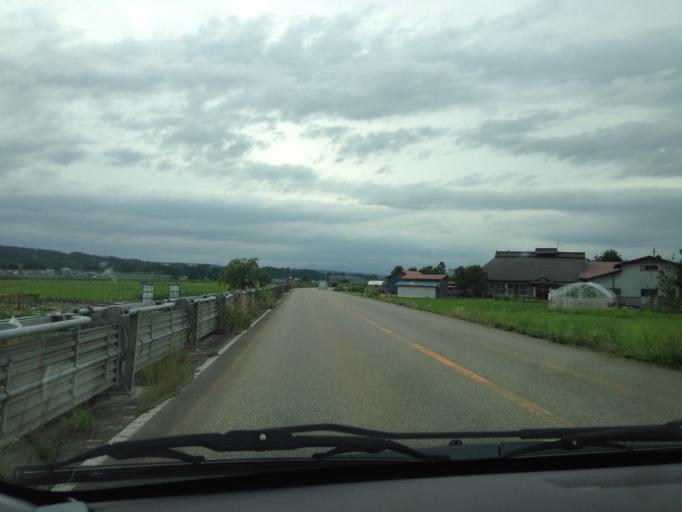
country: JP
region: Fukushima
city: Kitakata
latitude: 37.4847
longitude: 139.8390
